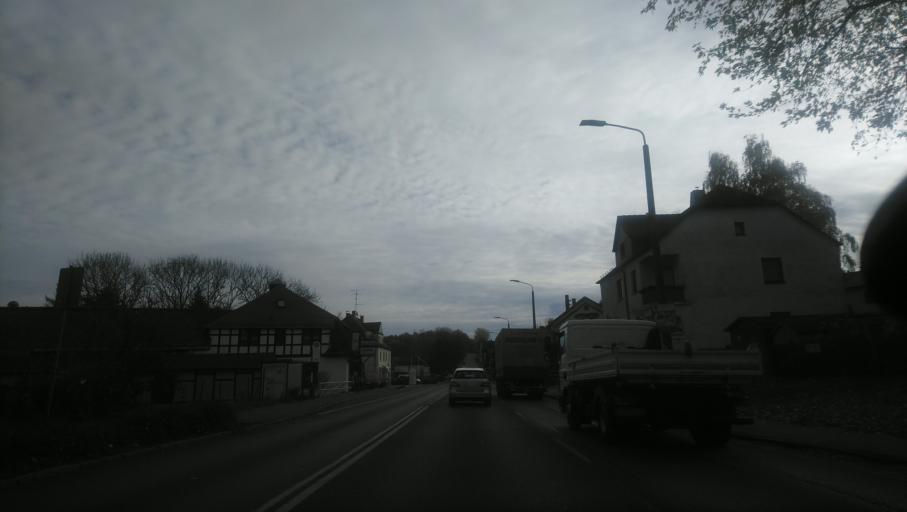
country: DE
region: Saxony
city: Wilkau-Hasslau
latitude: 50.7007
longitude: 12.5155
